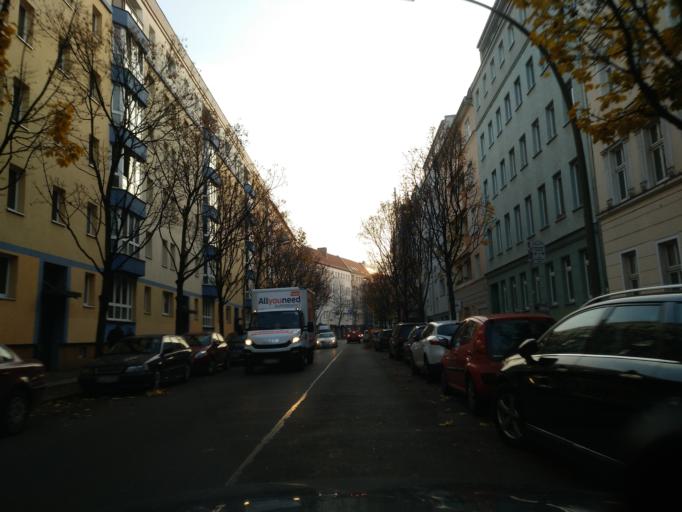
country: DE
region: Berlin
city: Friedrichshain Bezirk
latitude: 52.5138
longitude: 13.4672
